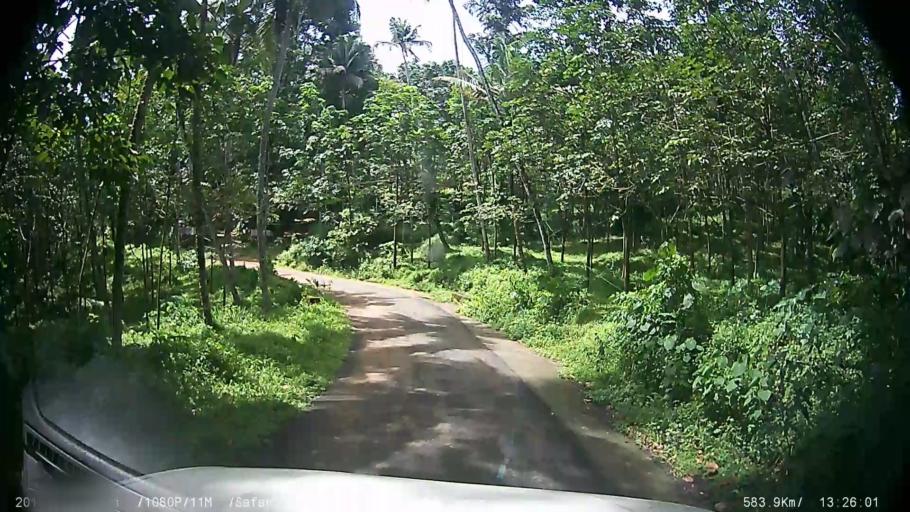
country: IN
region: Kerala
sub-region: Ernakulam
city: Muvattupuzha
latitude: 9.9216
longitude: 76.5660
